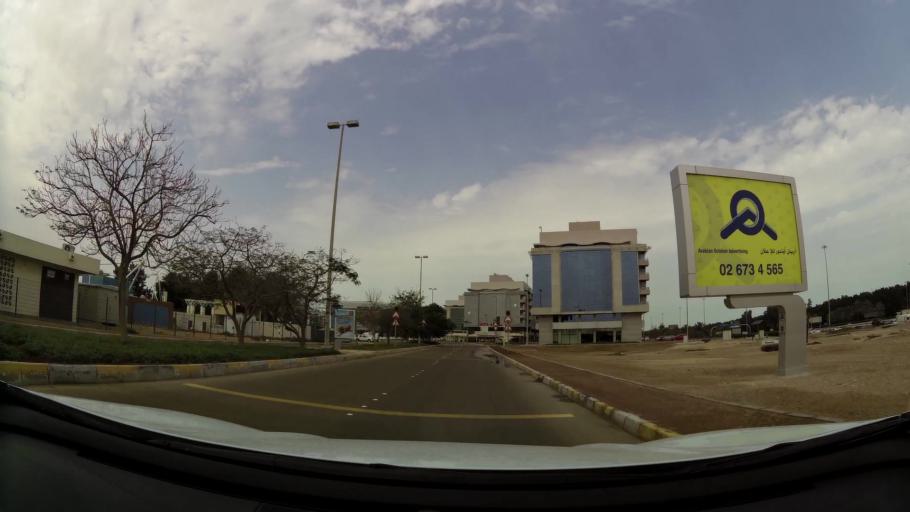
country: AE
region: Abu Dhabi
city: Abu Dhabi
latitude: 24.4290
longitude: 54.4690
